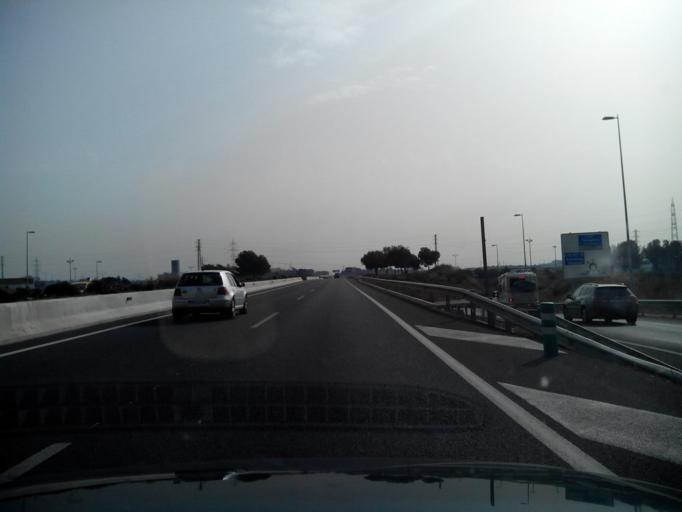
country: ES
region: Catalonia
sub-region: Provincia de Tarragona
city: Vila-seca
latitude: 41.1364
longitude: 1.1719
